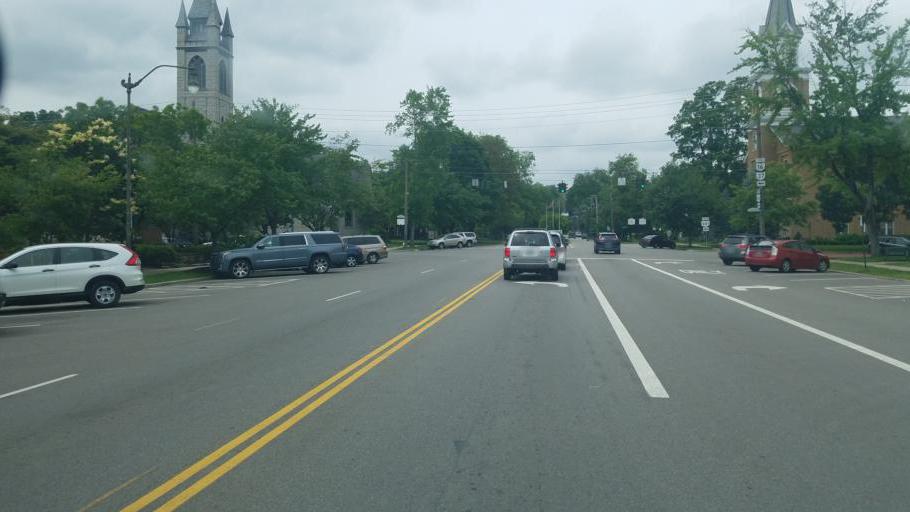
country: US
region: Ohio
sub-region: Licking County
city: Granville
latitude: 40.0680
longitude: -82.5194
